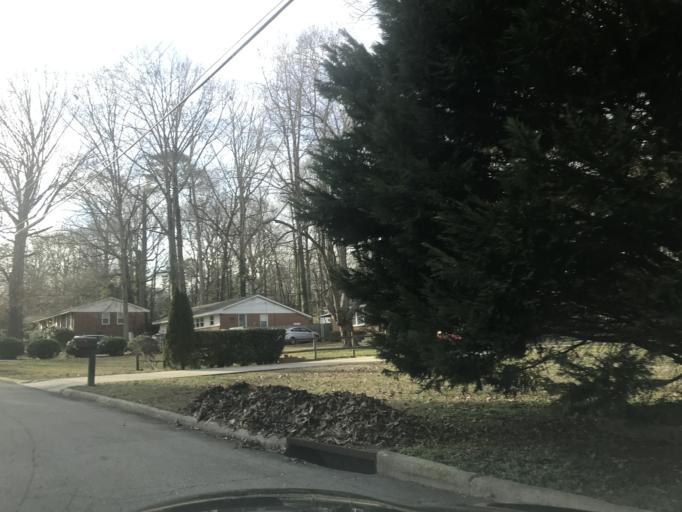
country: US
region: North Carolina
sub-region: Wake County
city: Raleigh
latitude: 35.8257
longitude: -78.5987
